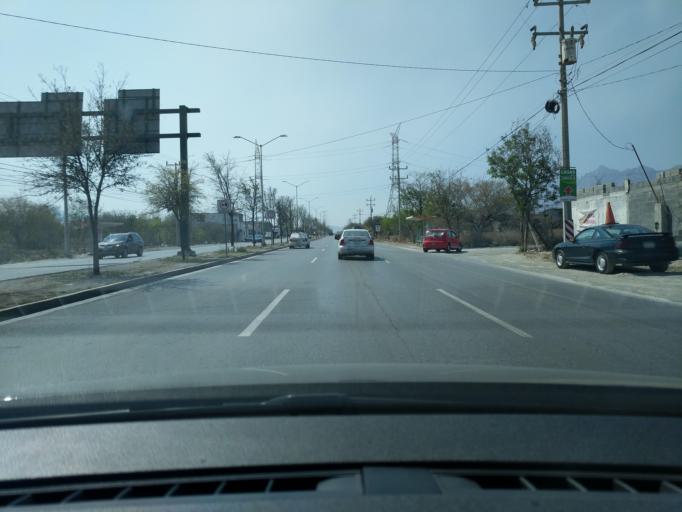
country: MX
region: Nuevo Leon
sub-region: Garcia
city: Valle de Lincoln
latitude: 25.7900
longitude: -100.4993
